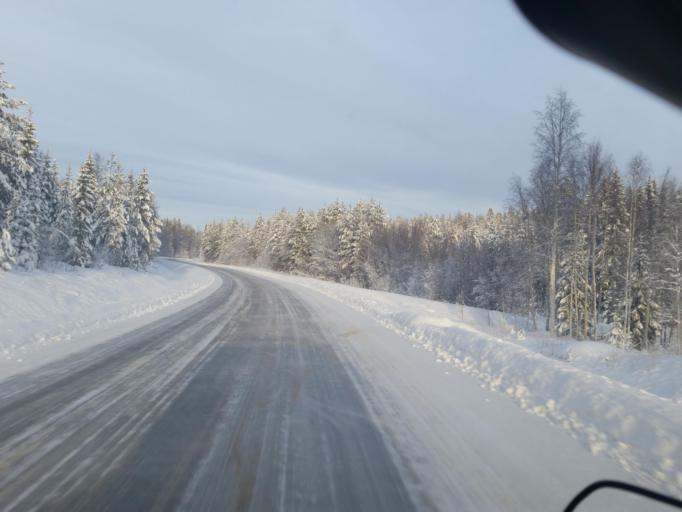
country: SE
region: Norrbotten
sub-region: Pitea Kommun
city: Norrfjarden
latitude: 65.4678
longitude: 21.4713
